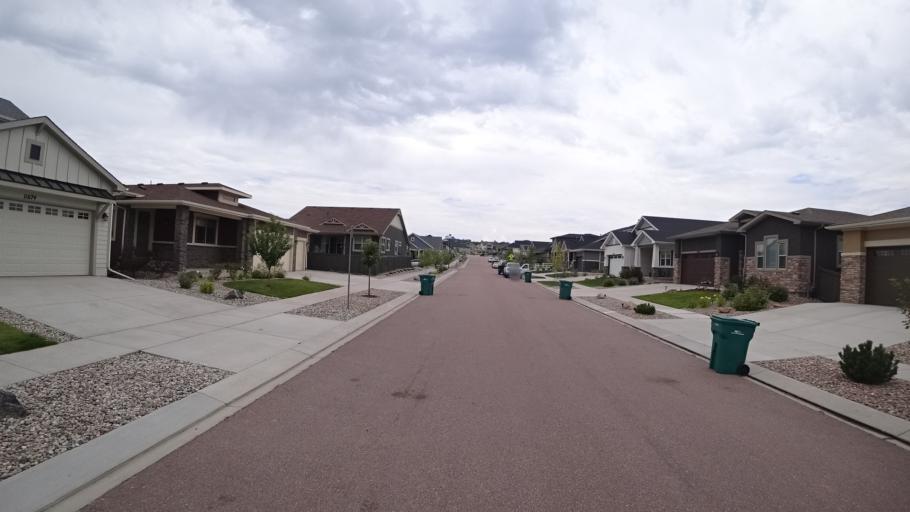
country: US
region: Colorado
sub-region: El Paso County
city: Gleneagle
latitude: 39.0009
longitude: -104.8044
